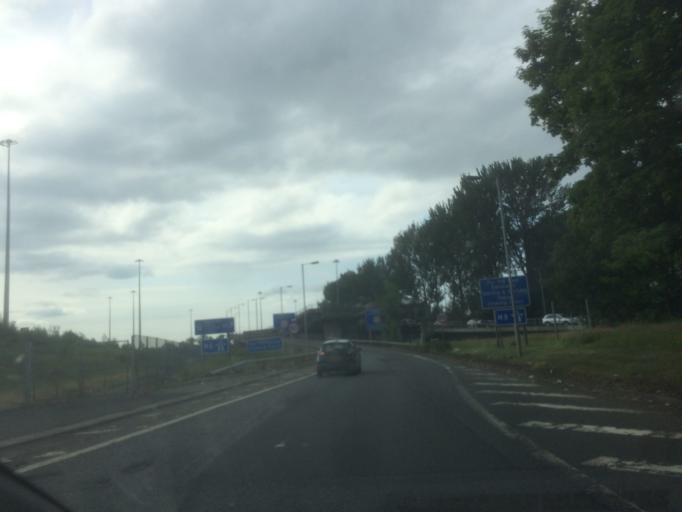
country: GB
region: Scotland
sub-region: Glasgow City
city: Glasgow
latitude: 55.8515
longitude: -4.2656
